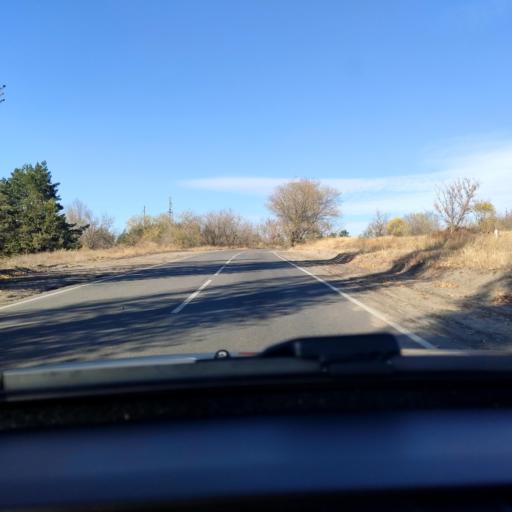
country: RU
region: Voronezj
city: Shilovo
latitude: 51.5520
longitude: 39.1337
